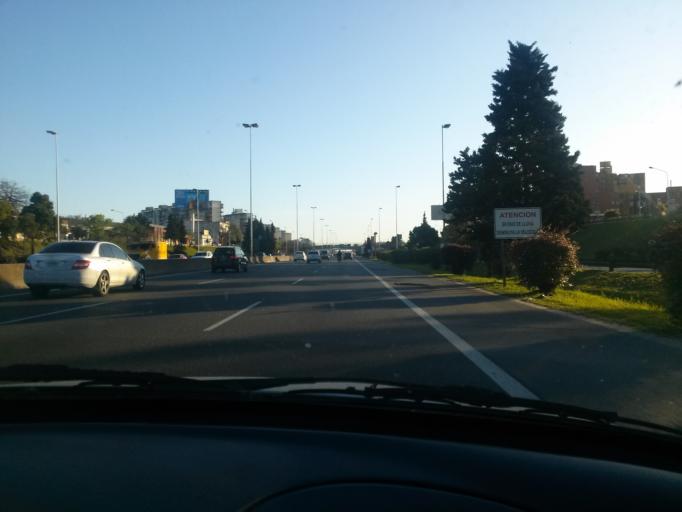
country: AR
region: Buenos Aires F.D.
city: Villa Lugano
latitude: -34.6920
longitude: -58.4896
